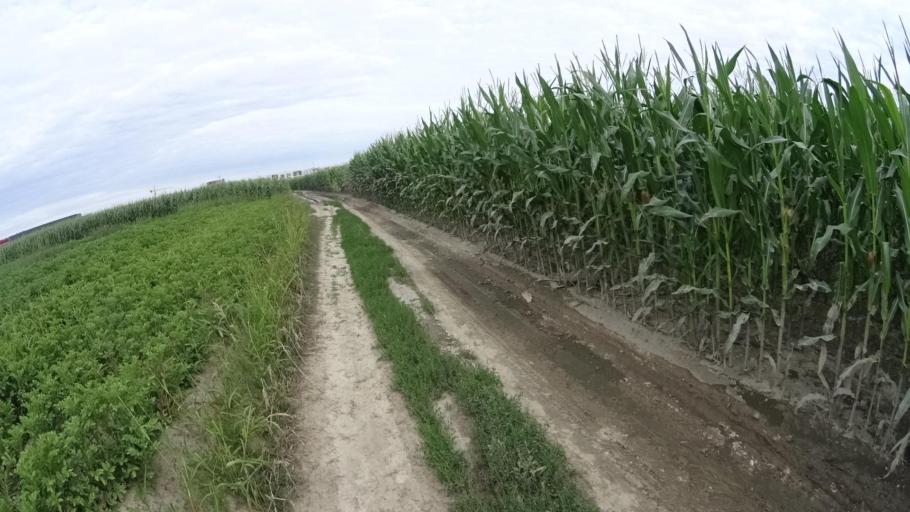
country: PL
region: Masovian Voivodeship
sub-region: Powiat warszawski zachodni
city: Babice
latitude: 52.2326
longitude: 20.8768
